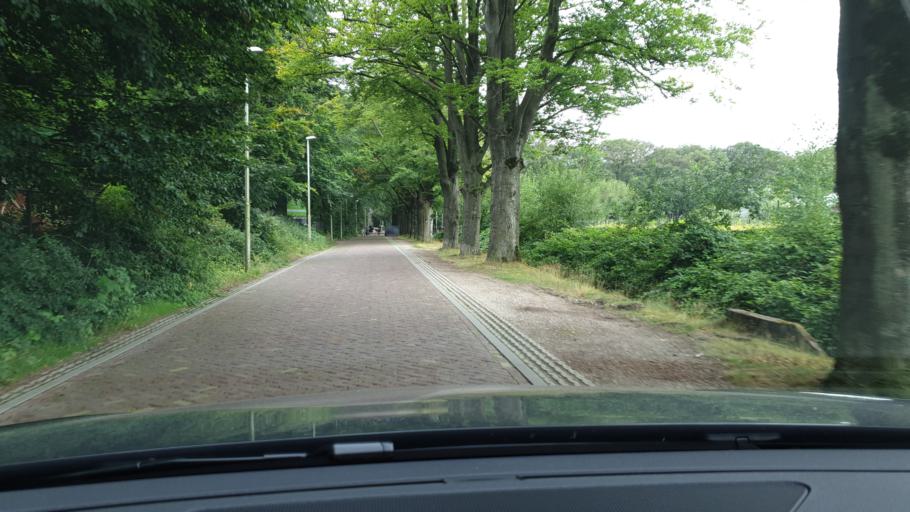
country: NL
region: North Brabant
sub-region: Gemeente Eindhoven
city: Meerhoven
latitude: 51.4640
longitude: 5.4293
